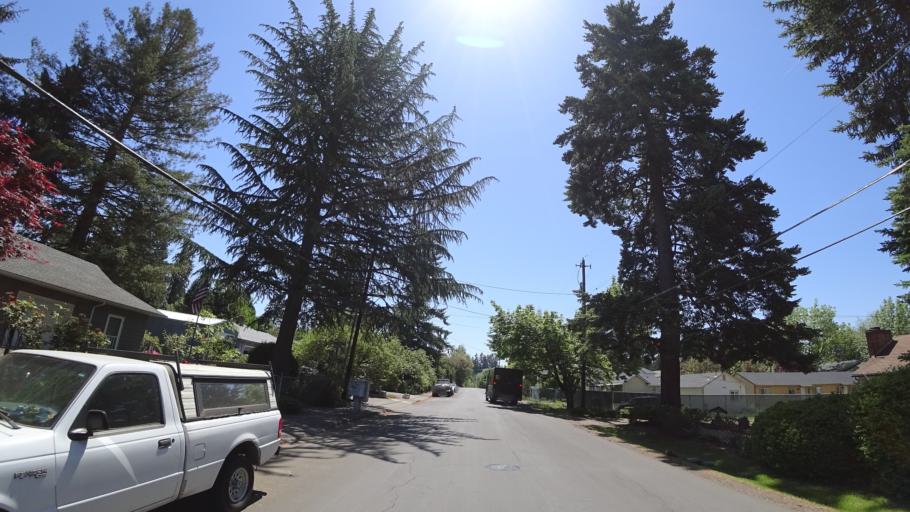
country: US
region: Oregon
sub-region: Washington County
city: Beaverton
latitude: 45.4841
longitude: -122.8300
